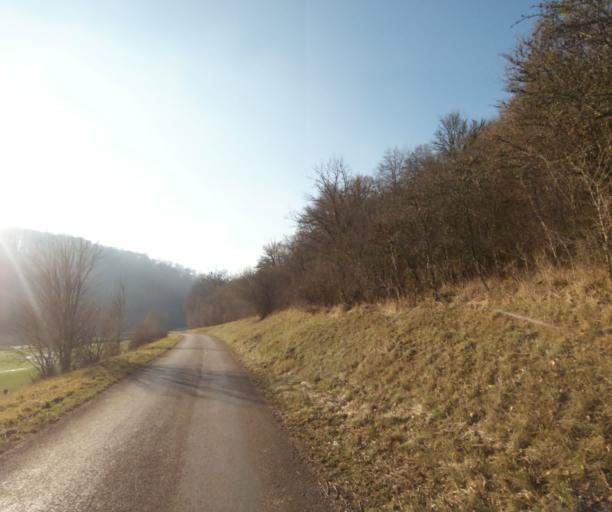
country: FR
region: Champagne-Ardenne
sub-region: Departement de la Haute-Marne
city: Joinville
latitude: 48.4902
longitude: 5.2079
